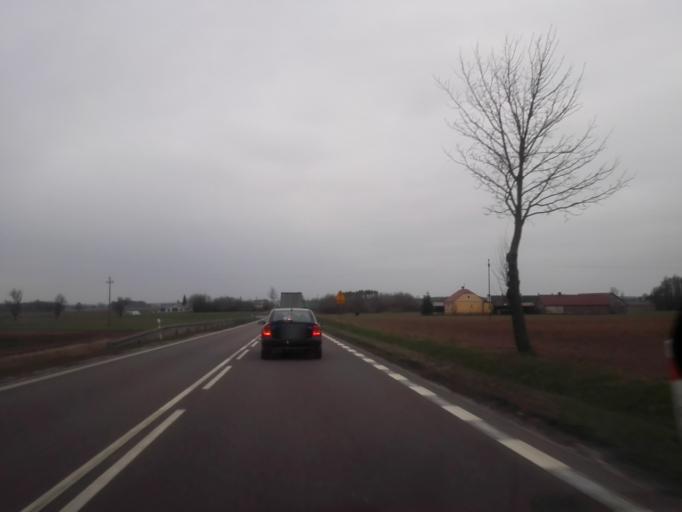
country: PL
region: Podlasie
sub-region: Powiat grajewski
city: Szczuczyn
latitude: 53.5889
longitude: 22.3322
